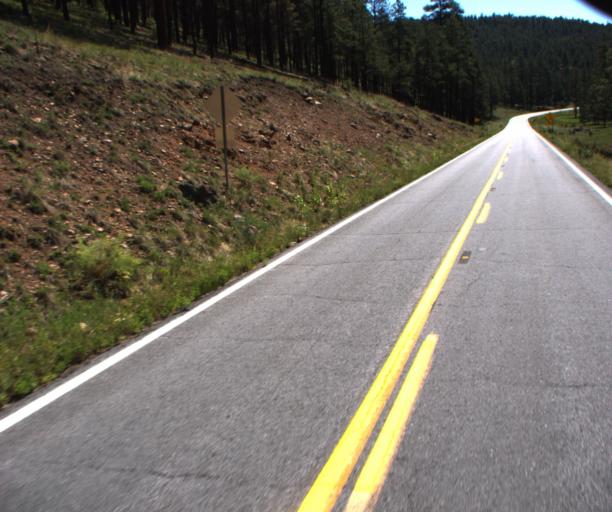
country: US
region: Arizona
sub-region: Apache County
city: Eagar
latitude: 33.7476
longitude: -109.2092
